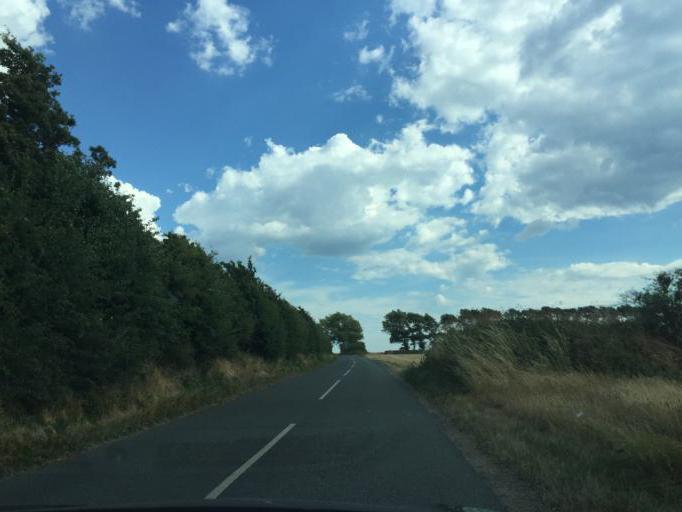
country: DK
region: South Denmark
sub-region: Assens Kommune
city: Harby
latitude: 55.1613
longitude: 9.9921
